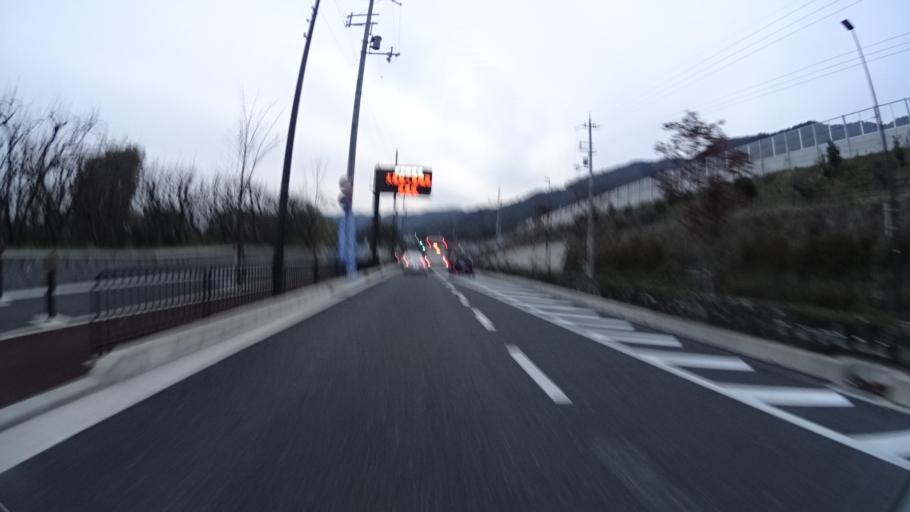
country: JP
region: Kyoto
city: Muko
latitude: 34.9673
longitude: 135.6580
